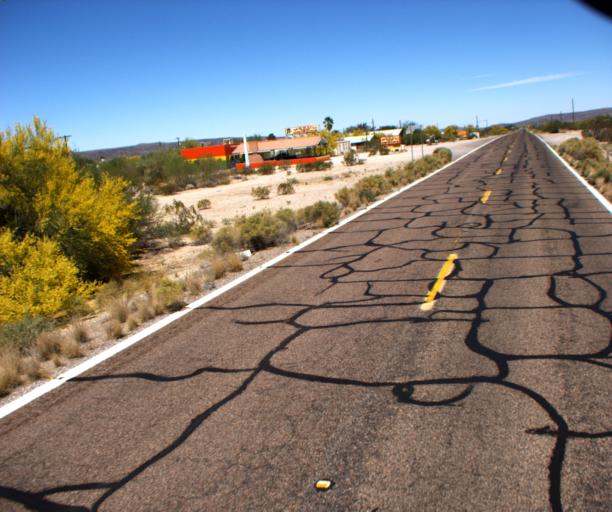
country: US
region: Arizona
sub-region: Pima County
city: Ajo
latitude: 32.4221
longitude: -112.8715
